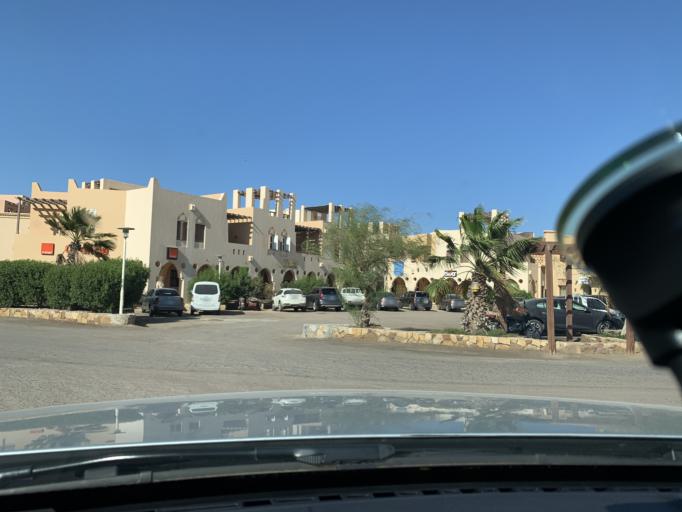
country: EG
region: Red Sea
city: El Gouna
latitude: 27.4075
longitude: 33.6732
